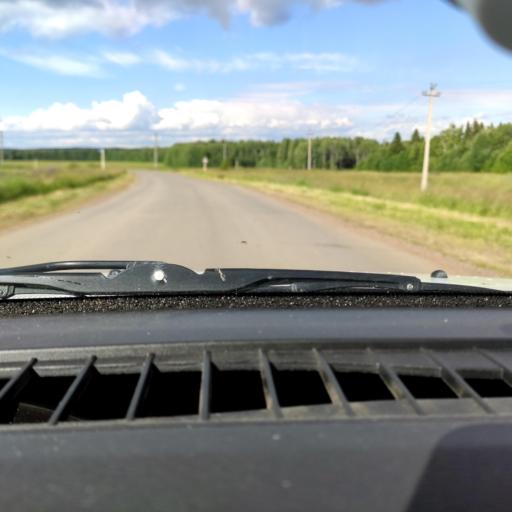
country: RU
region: Perm
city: Uinskoye
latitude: 57.1419
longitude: 56.5675
